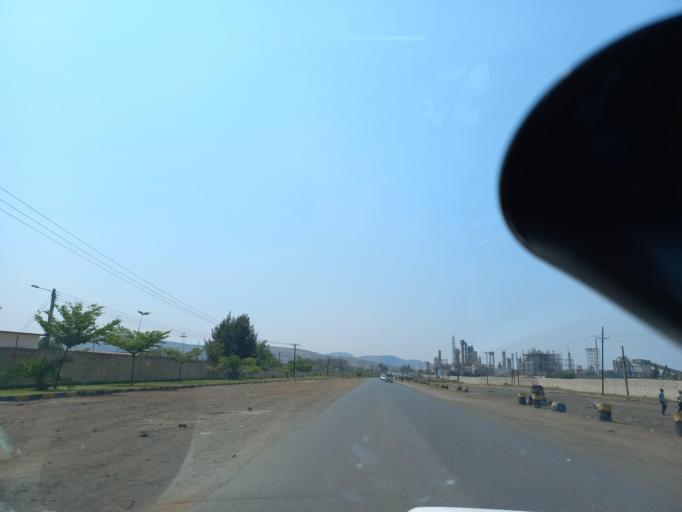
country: ZM
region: Lusaka
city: Kafue
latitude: -15.7517
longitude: 28.1641
